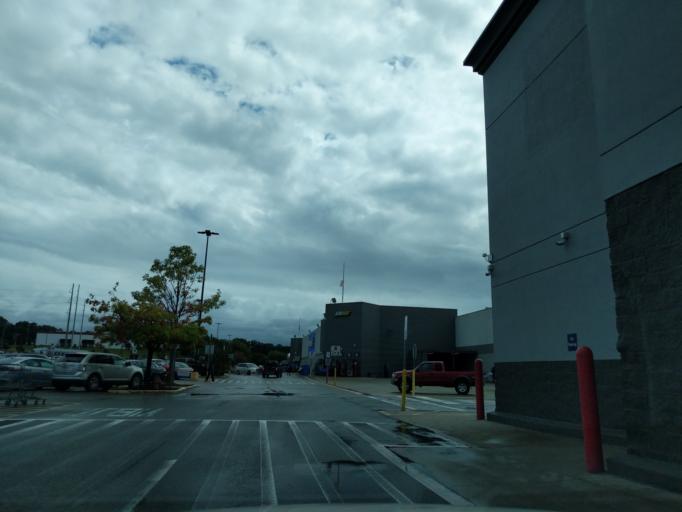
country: US
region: Alabama
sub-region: Tuscaloosa County
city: Tuscaloosa
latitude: 33.1659
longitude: -87.5199
